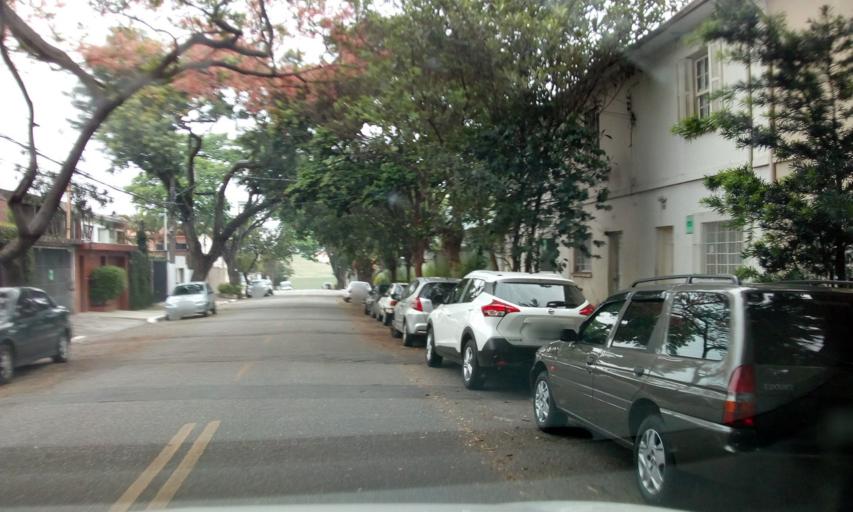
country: BR
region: Sao Paulo
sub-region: Sao Paulo
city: Sao Paulo
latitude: -23.6164
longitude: -46.6577
